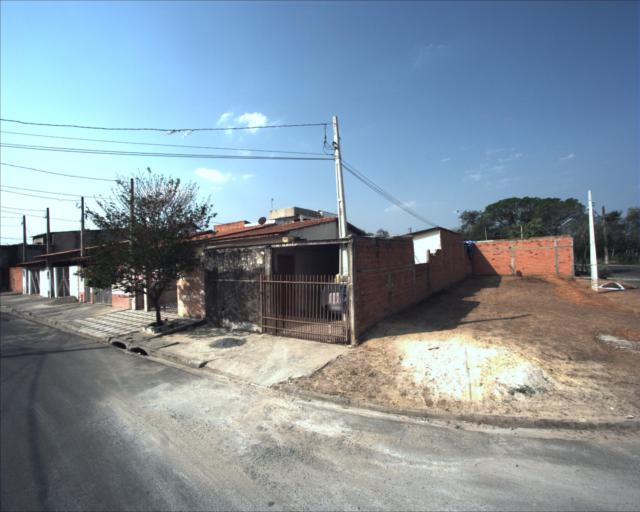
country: BR
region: Sao Paulo
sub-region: Sorocaba
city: Sorocaba
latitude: -23.4346
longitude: -47.4546
